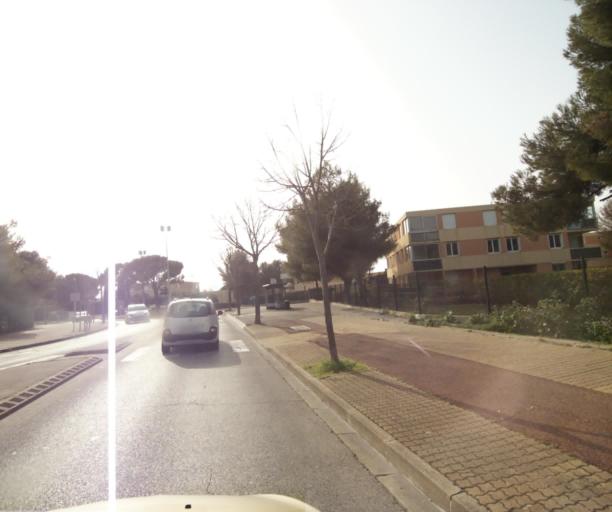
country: FR
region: Provence-Alpes-Cote d'Azur
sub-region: Departement des Bouches-du-Rhone
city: Vitrolles
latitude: 43.4583
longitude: 5.2423
